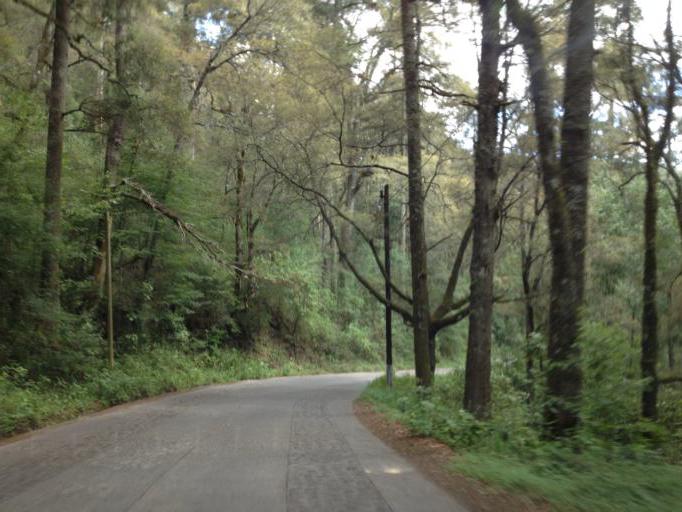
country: MX
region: Hidalgo
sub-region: Pachuca de Soto
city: San Miguel Cerezo (El Cerezo)
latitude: 20.2190
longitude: -98.7146
